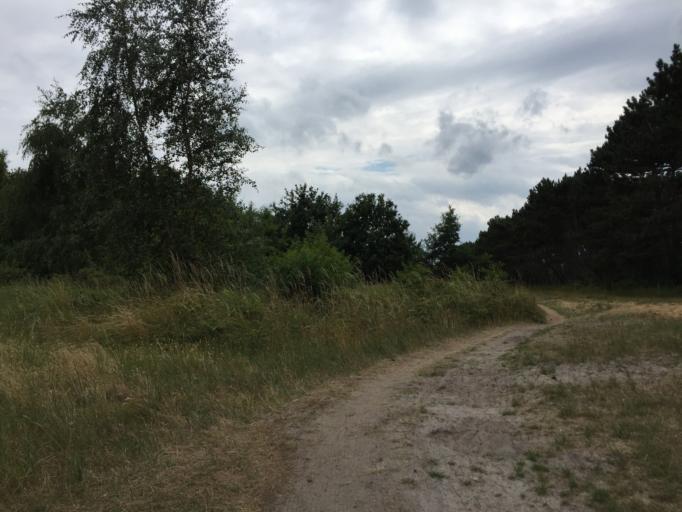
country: DE
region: Mecklenburg-Vorpommern
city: Hiddensee
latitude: 54.5148
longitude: 13.0796
